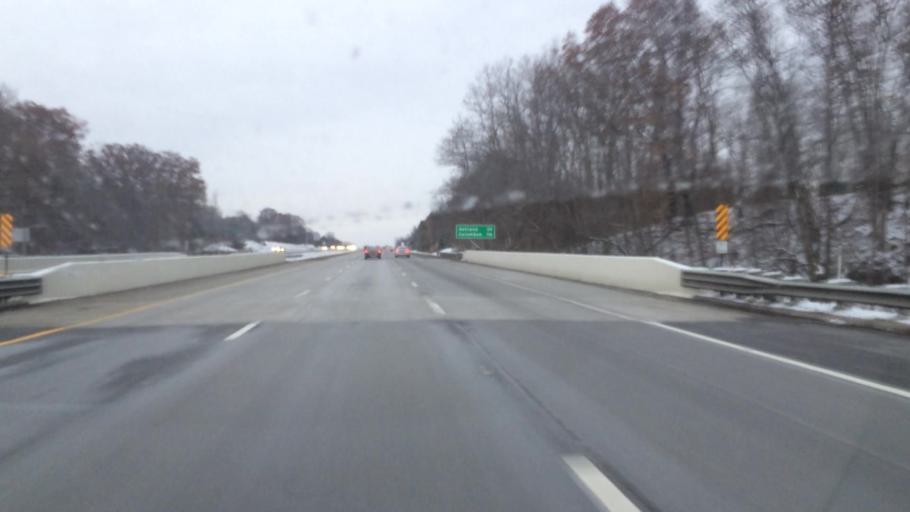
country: US
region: Ohio
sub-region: Medina County
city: Brunswick
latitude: 41.1801
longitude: -81.7882
